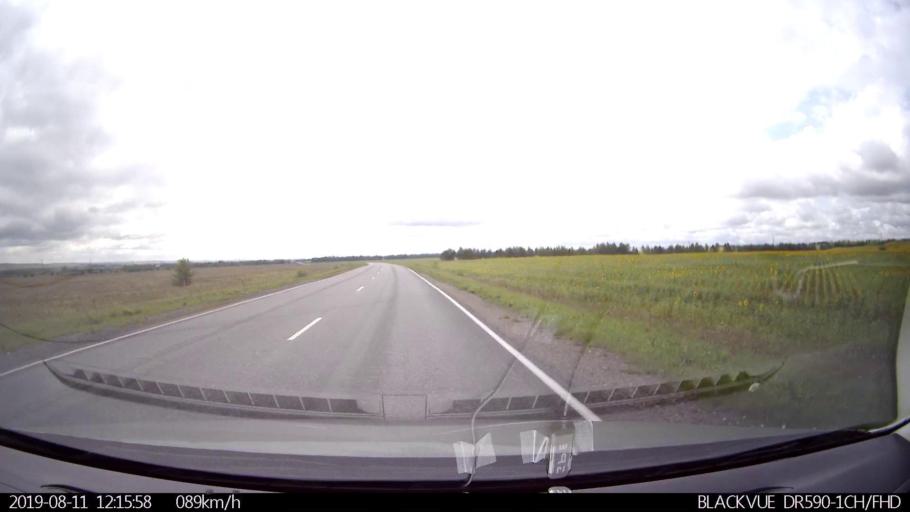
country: RU
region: Ulyanovsk
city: Ignatovka
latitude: 53.9357
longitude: 47.9632
